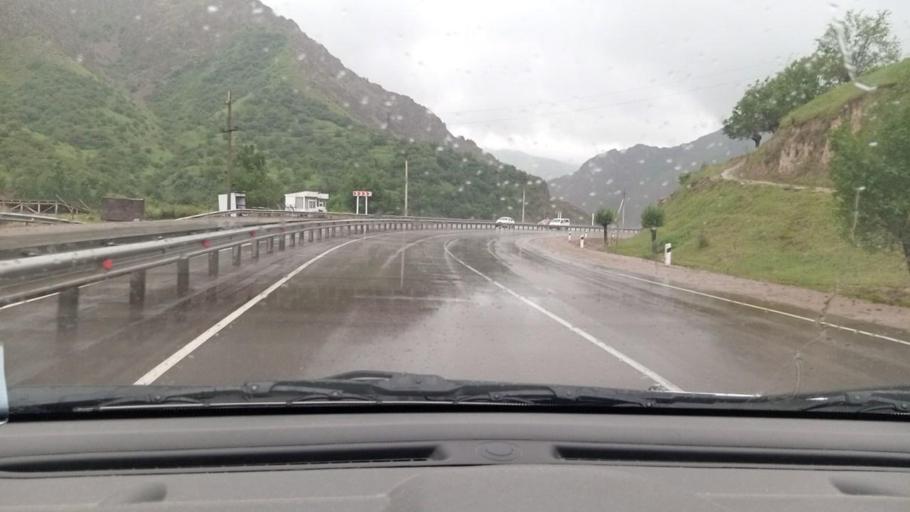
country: UZ
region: Toshkent
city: Angren
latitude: 41.1014
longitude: 70.3296
